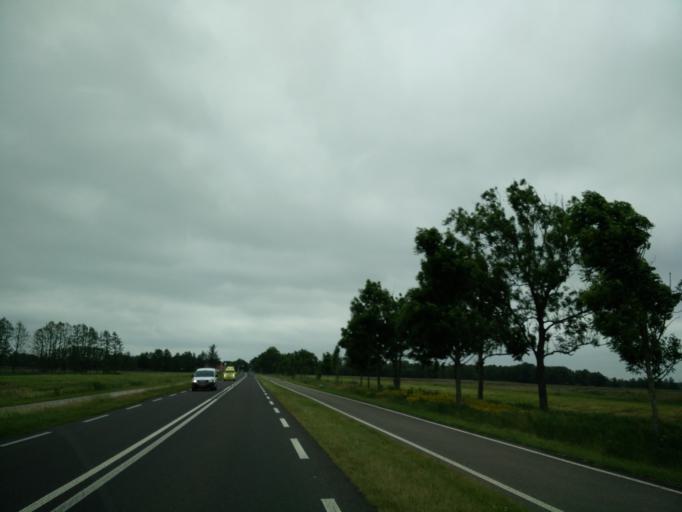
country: NL
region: Groningen
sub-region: Gemeente Groningen
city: Groningen
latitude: 53.1718
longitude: 6.4978
